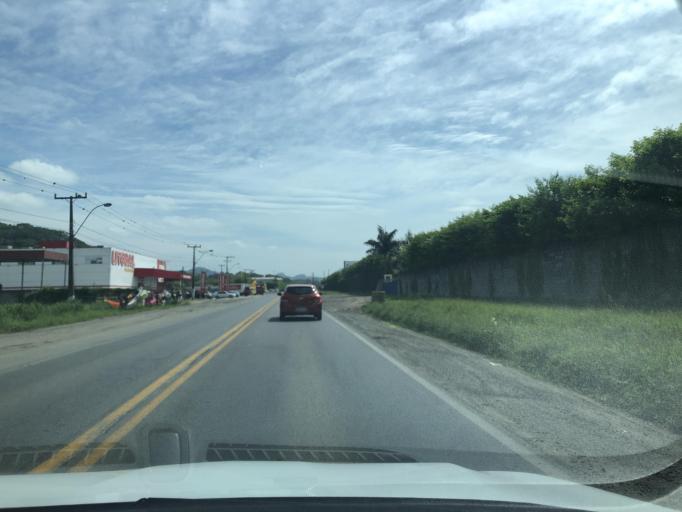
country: BR
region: Santa Catarina
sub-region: Sao Francisco Do Sul
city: Sao Francisco do Sul
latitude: -26.2557
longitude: -48.6213
